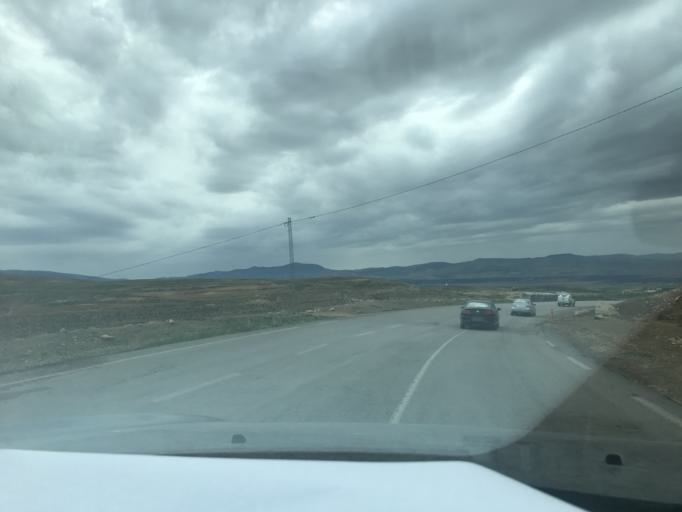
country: TN
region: Silyanah
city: Siliana
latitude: 36.0906
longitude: 9.4671
